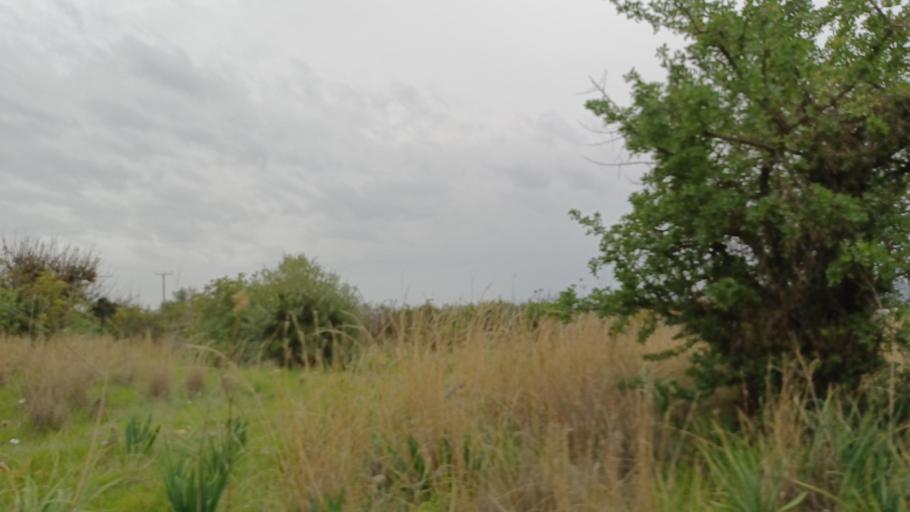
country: CY
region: Pafos
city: Polis
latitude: 35.0508
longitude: 32.4683
